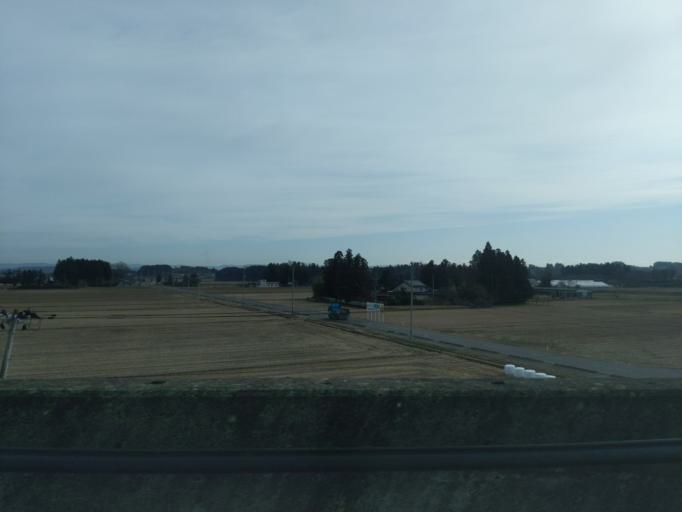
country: JP
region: Iwate
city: Ichinoseki
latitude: 38.7559
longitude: 141.0757
